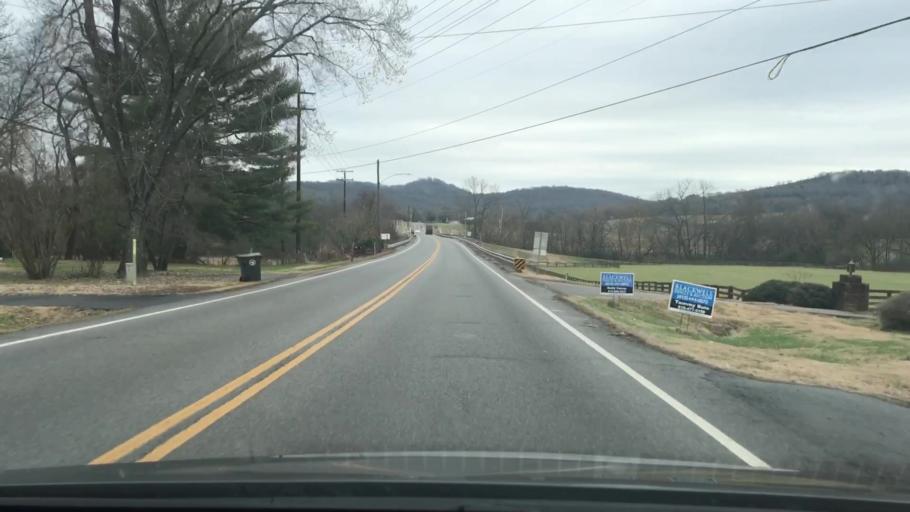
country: US
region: Tennessee
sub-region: Trousdale County
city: Hartsville
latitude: 36.3859
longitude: -86.1321
